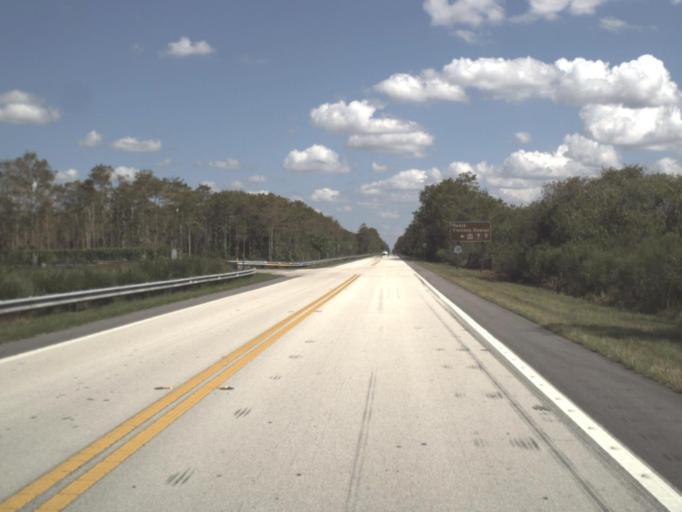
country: US
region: Florida
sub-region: Miami-Dade County
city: Kendall West
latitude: 25.8568
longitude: -81.0331
